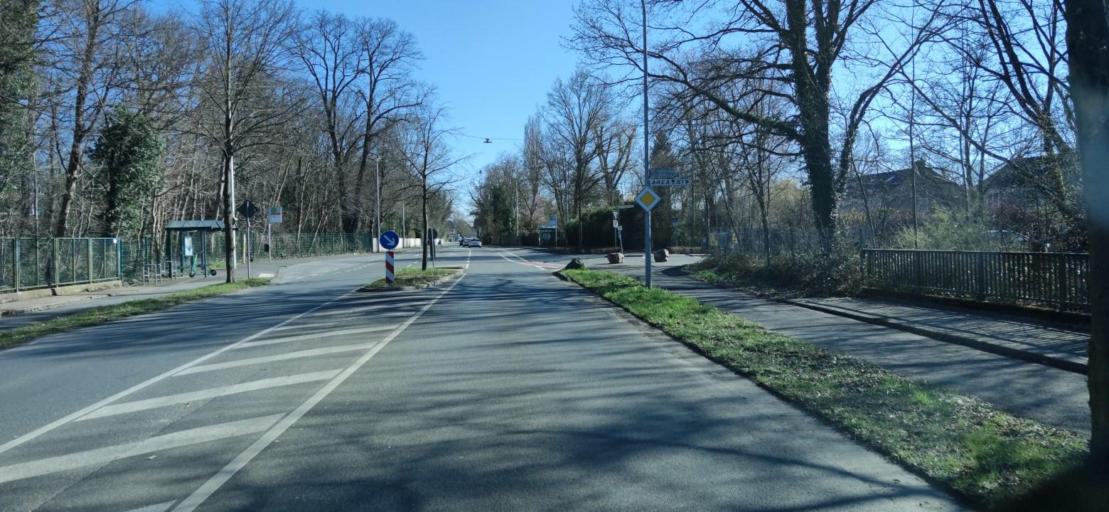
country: DE
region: North Rhine-Westphalia
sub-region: Regierungsbezirk Dusseldorf
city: Hilden
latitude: 51.1857
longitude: 6.9368
